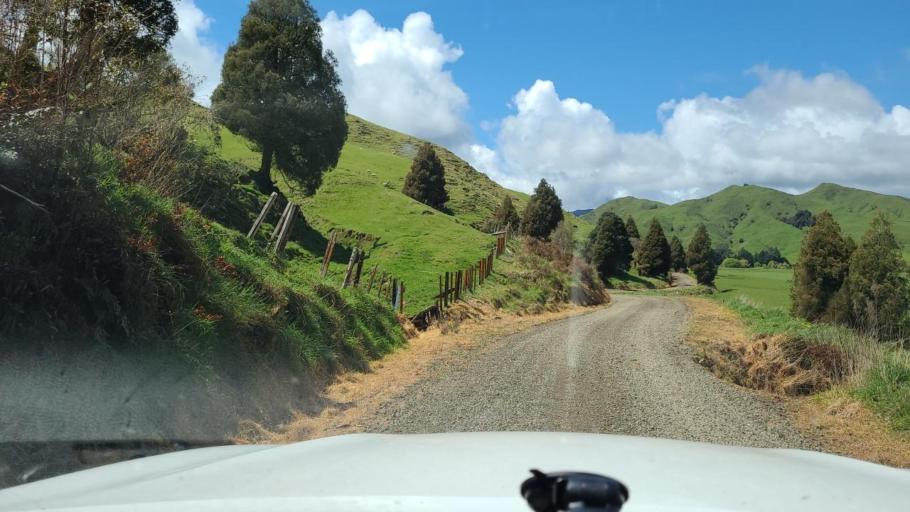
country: NZ
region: Bay of Plenty
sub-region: Opotiki District
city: Opotiki
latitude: -38.2528
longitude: 177.5568
